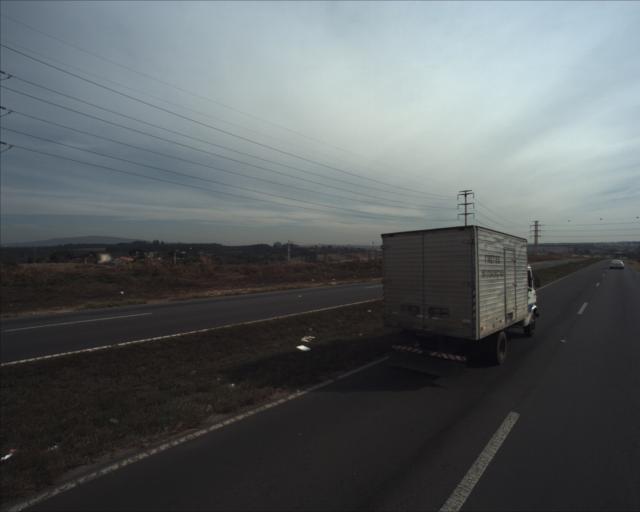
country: BR
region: Sao Paulo
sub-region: Sorocaba
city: Sorocaba
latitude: -23.4487
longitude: -47.5137
